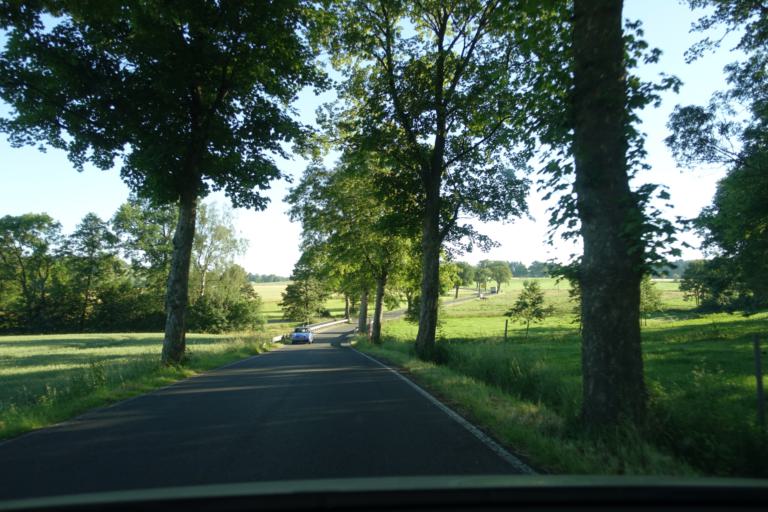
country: DE
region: Saxony
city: Eppendorf
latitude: 50.7930
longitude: 13.2833
